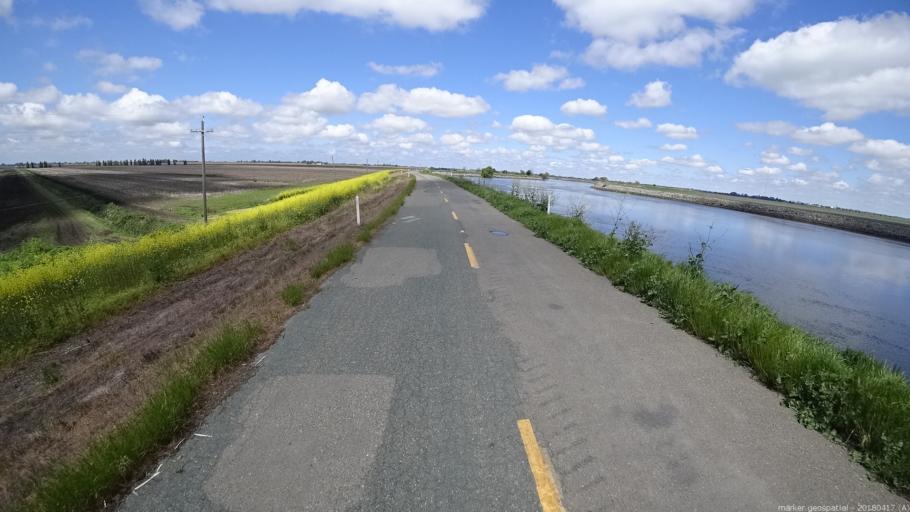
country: US
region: California
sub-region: Sacramento County
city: Walnut Grove
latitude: 38.1750
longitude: -121.5255
